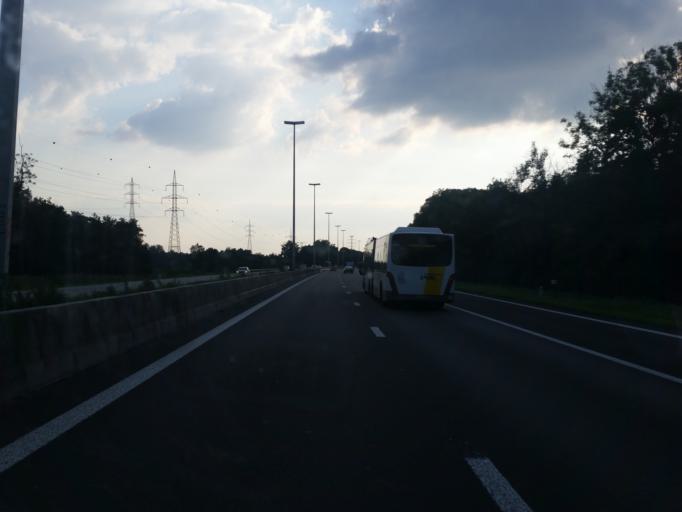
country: BE
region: Flanders
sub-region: Provincie Antwerpen
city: Zandhoven
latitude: 51.2184
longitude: 4.6393
